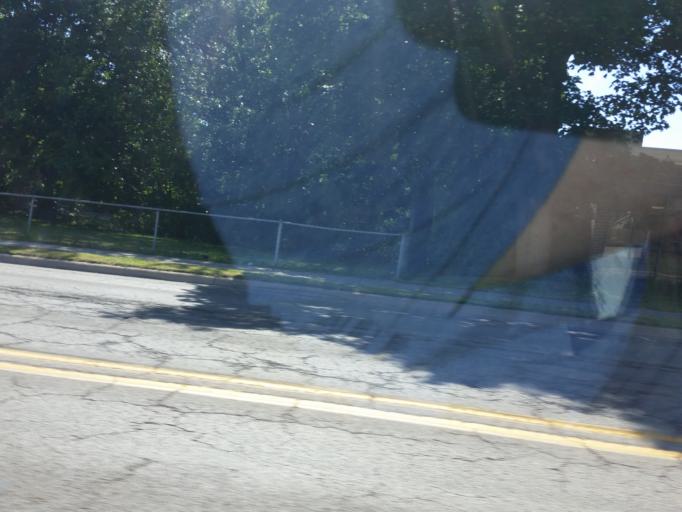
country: US
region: Illinois
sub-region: Winnebago County
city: Rockford
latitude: 42.2546
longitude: -89.0720
